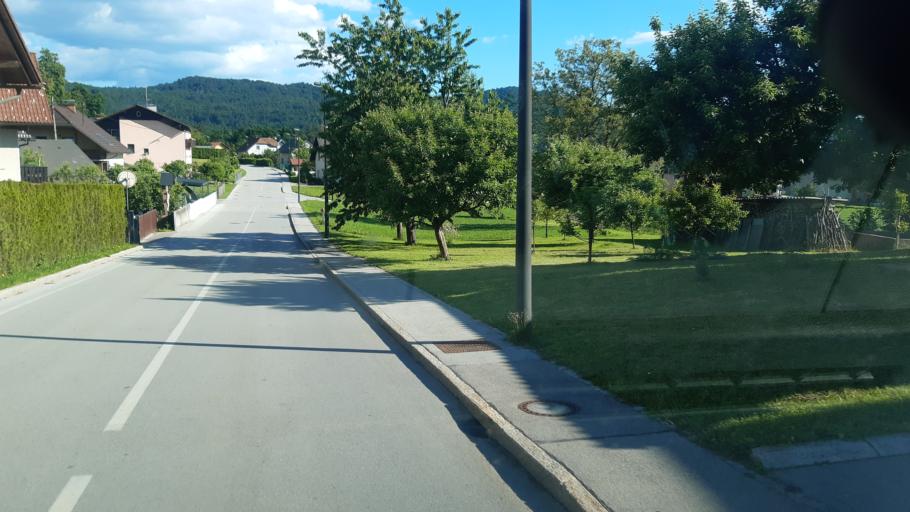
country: SI
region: Vodice
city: Vodice
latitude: 46.1717
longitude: 14.5096
